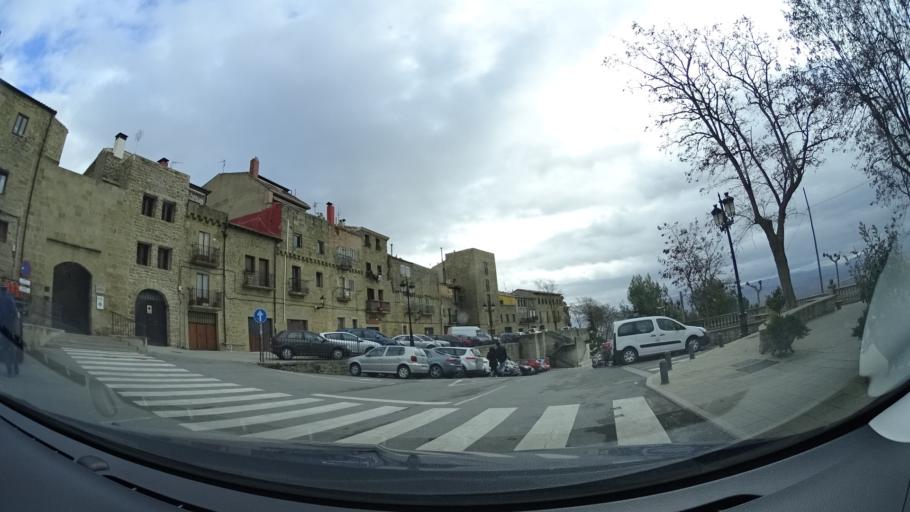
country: ES
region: Basque Country
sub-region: Provincia de Alava
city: Laguardia
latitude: 42.5538
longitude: -2.5862
